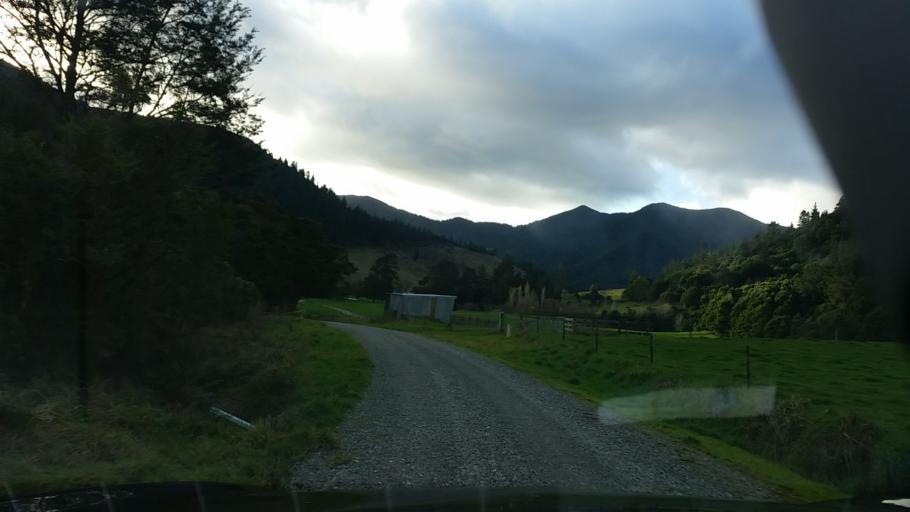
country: NZ
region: Marlborough
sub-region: Marlborough District
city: Picton
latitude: -41.1733
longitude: 173.6510
